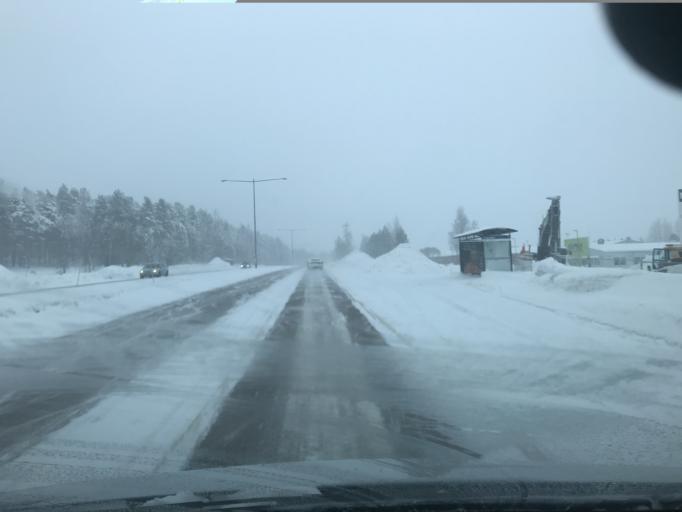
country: SE
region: Norrbotten
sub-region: Lulea Kommun
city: Lulea
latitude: 65.6107
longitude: 22.1357
